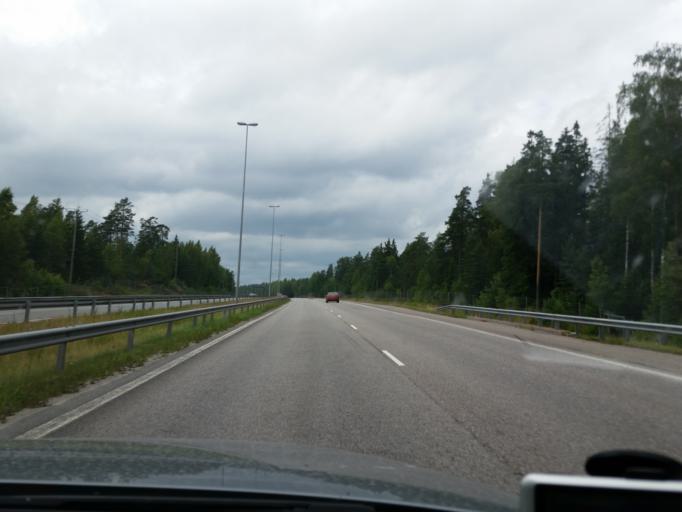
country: FI
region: Uusimaa
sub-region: Helsinki
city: Espoo
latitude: 60.2505
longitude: 24.5357
